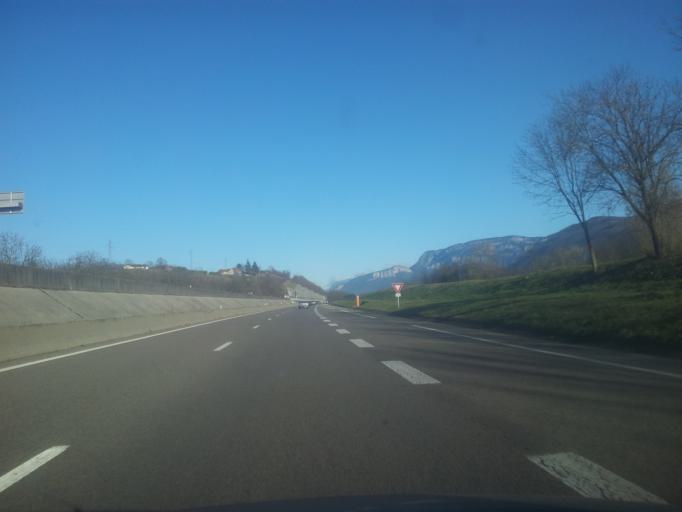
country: FR
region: Rhone-Alpes
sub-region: Departement de l'Isere
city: Saint-Sauveur
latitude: 45.1610
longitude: 5.3639
